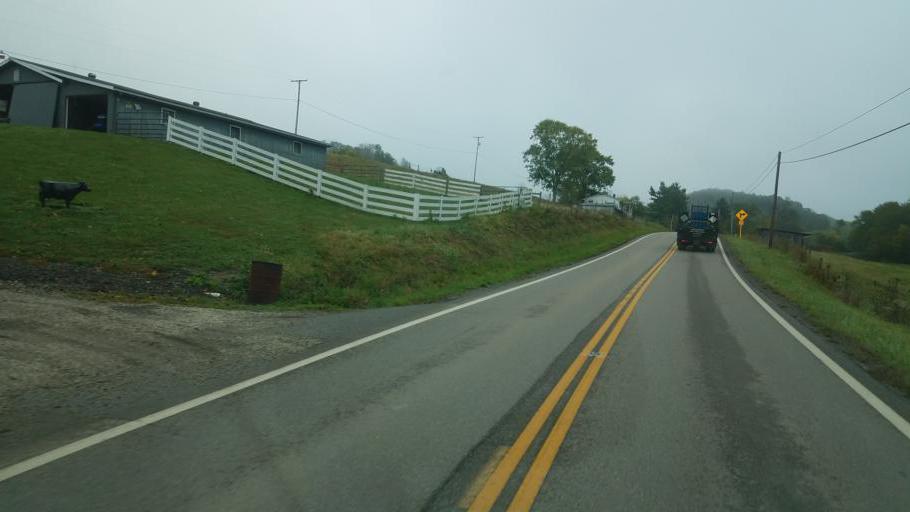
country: US
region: Ohio
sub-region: Tuscarawas County
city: Rockford
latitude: 40.4297
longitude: -81.1775
